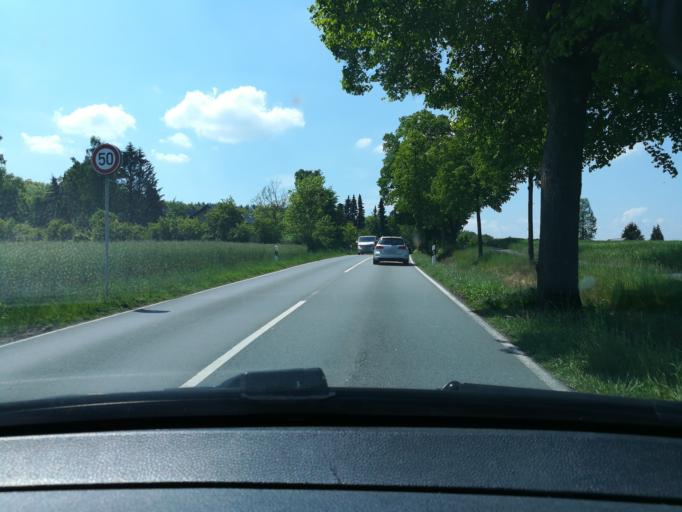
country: DE
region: North Rhine-Westphalia
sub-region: Regierungsbezirk Detmold
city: Bad Salzuflen
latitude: 52.1260
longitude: 8.7221
